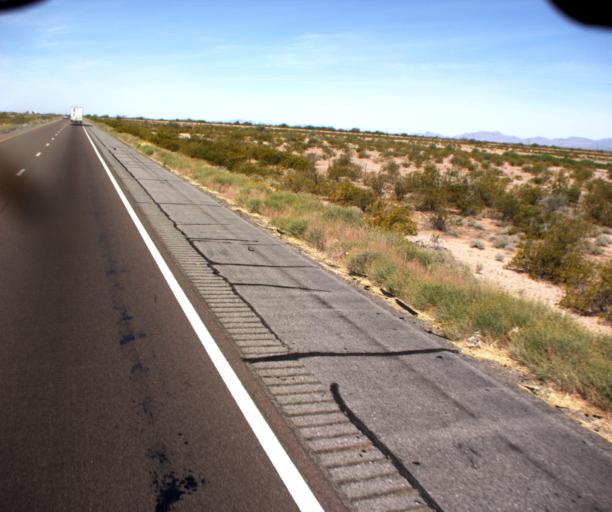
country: US
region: Arizona
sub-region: La Paz County
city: Salome
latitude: 33.5509
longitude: -113.2316
